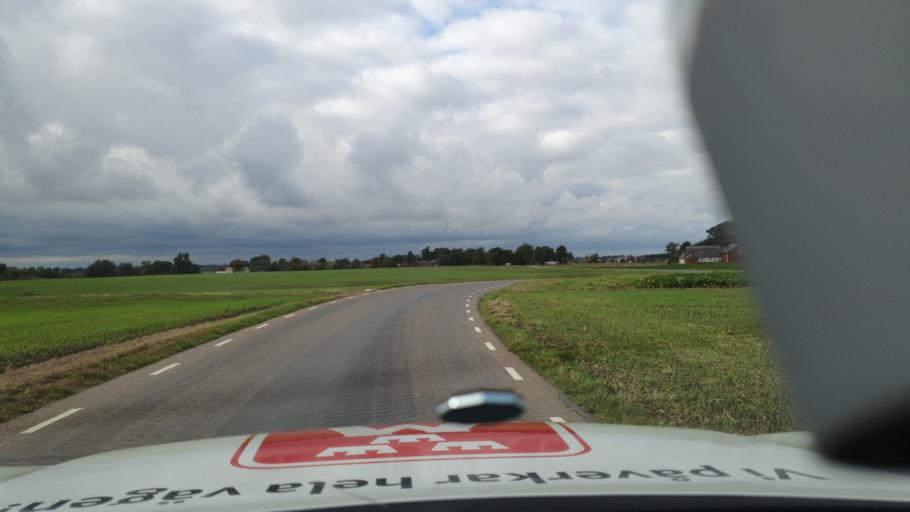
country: SE
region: Skane
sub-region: Trelleborgs Kommun
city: Skare
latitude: 55.4246
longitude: 13.0973
